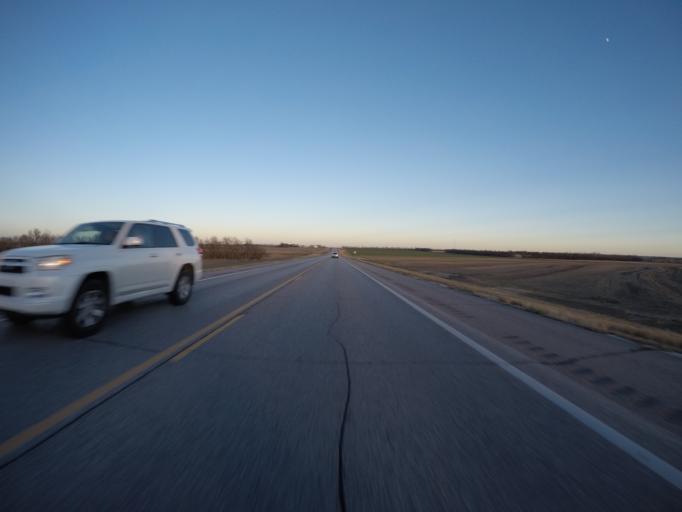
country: US
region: Kansas
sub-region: Marion County
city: Peabody
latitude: 38.1746
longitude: -97.1597
